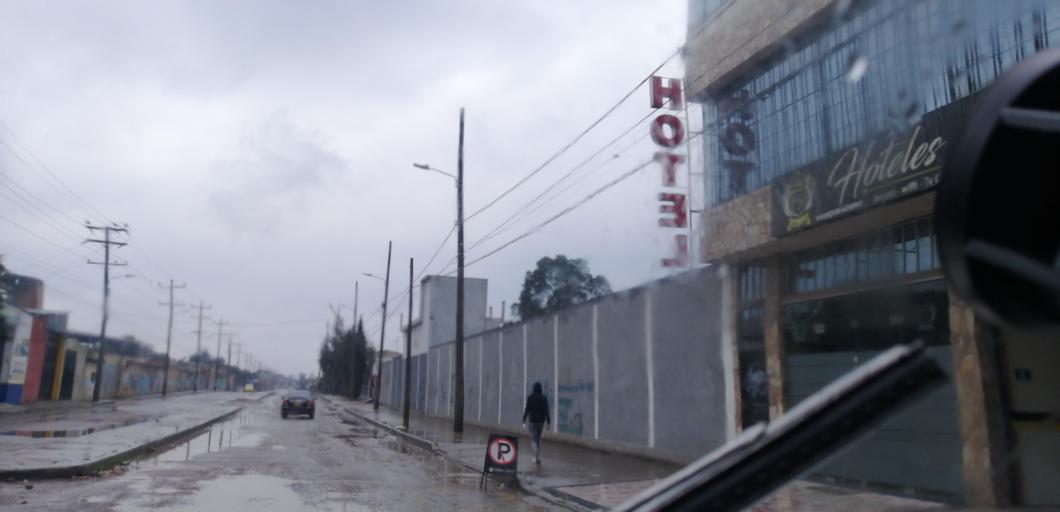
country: CO
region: Cundinamarca
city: Madrid
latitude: 4.7395
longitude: -74.2622
